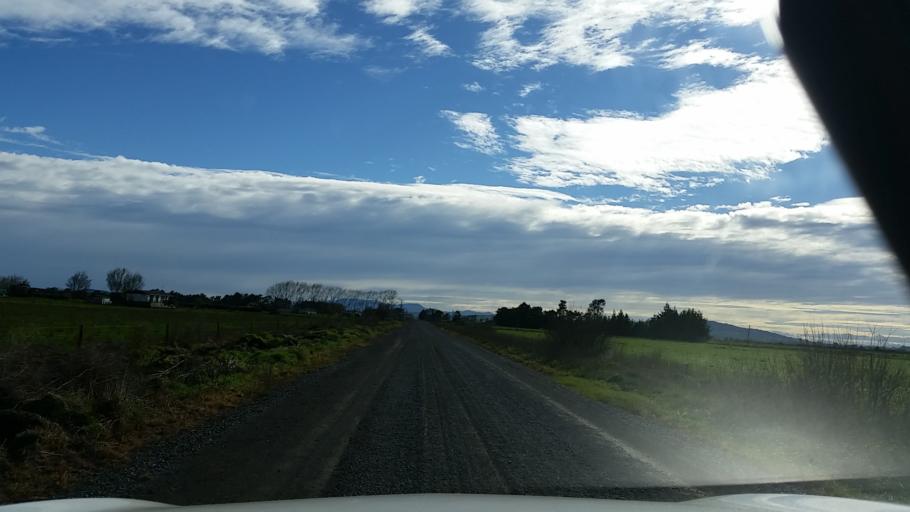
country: NZ
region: Waikato
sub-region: Hamilton City
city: Hamilton
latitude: -37.6730
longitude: 175.4410
